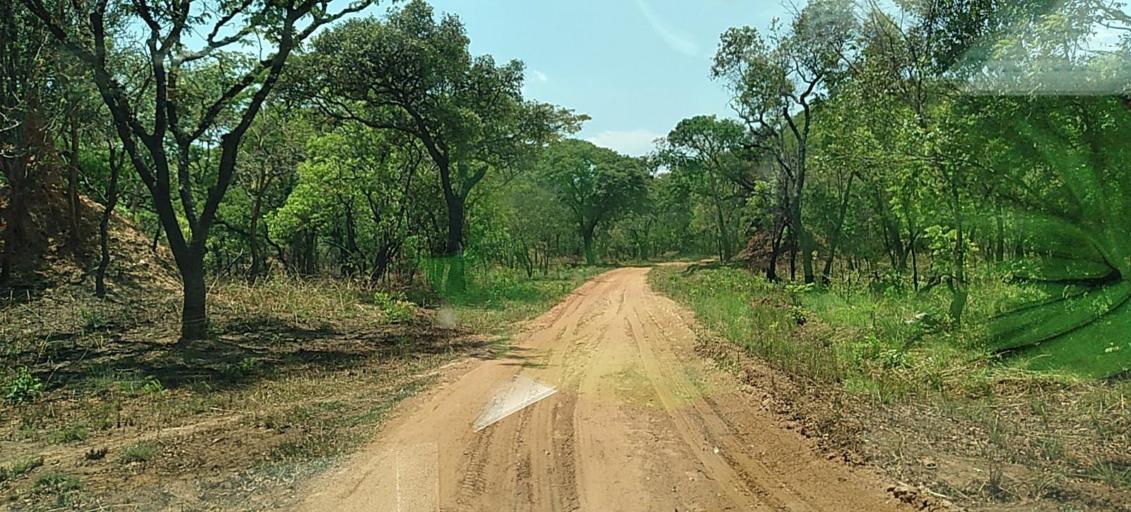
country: CD
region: Katanga
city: Kolwezi
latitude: -11.3602
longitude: 25.2061
